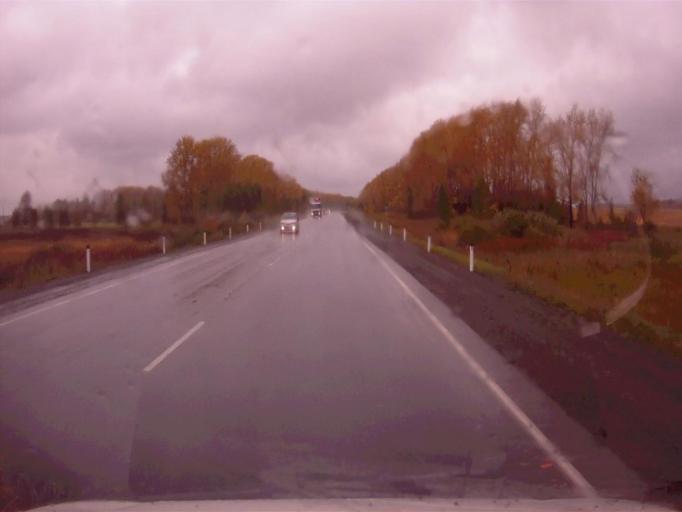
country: RU
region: Chelyabinsk
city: Argayash
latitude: 55.4476
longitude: 60.9453
